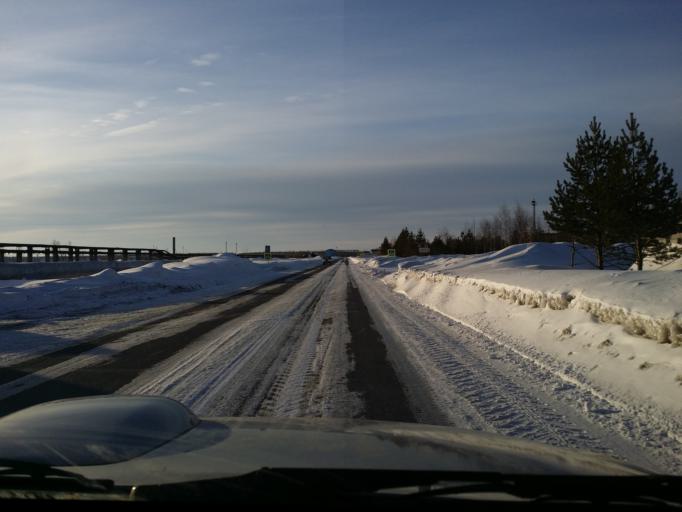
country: RU
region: Khanty-Mansiyskiy Avtonomnyy Okrug
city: Izluchinsk
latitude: 60.9780
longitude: 76.9239
